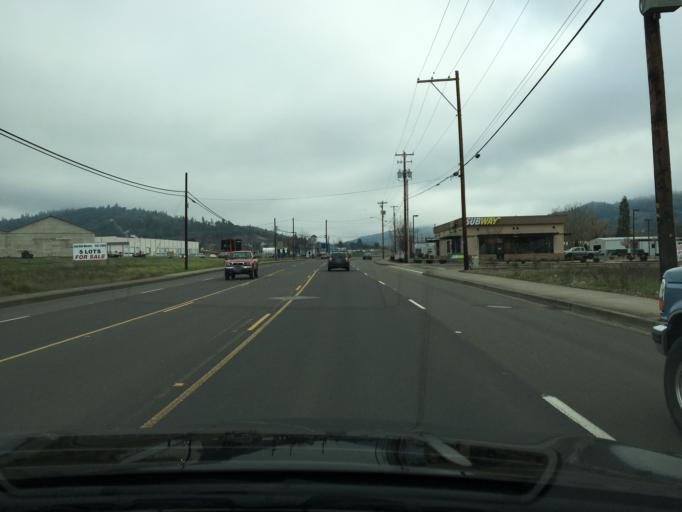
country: US
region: Oregon
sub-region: Douglas County
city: Roseburg
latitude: 43.2133
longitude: -123.3350
